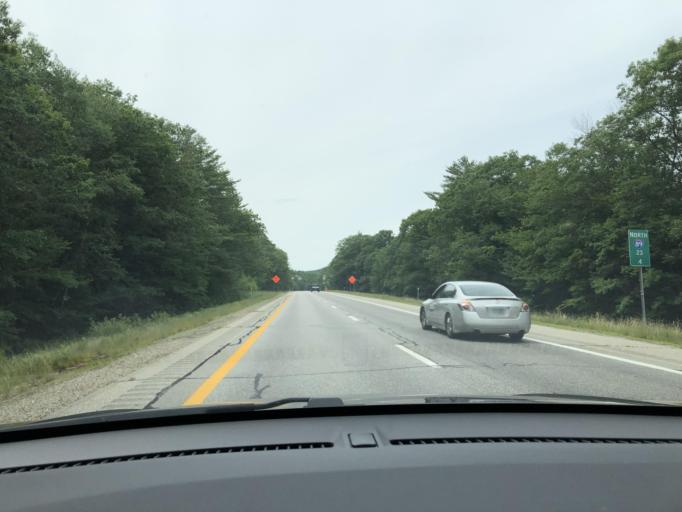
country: US
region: New Hampshire
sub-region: Merrimack County
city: Sutton
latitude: 43.3190
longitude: -71.8786
